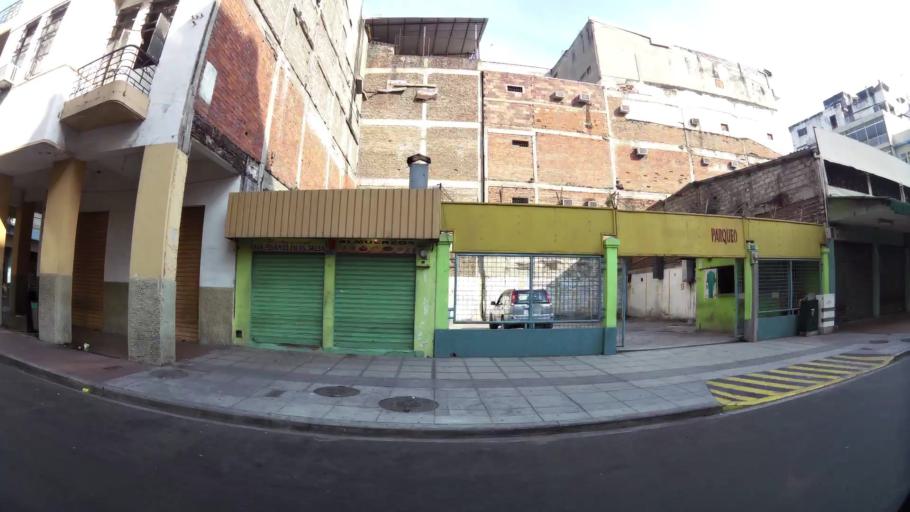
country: EC
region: Guayas
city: Guayaquil
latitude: -2.1903
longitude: -79.8827
